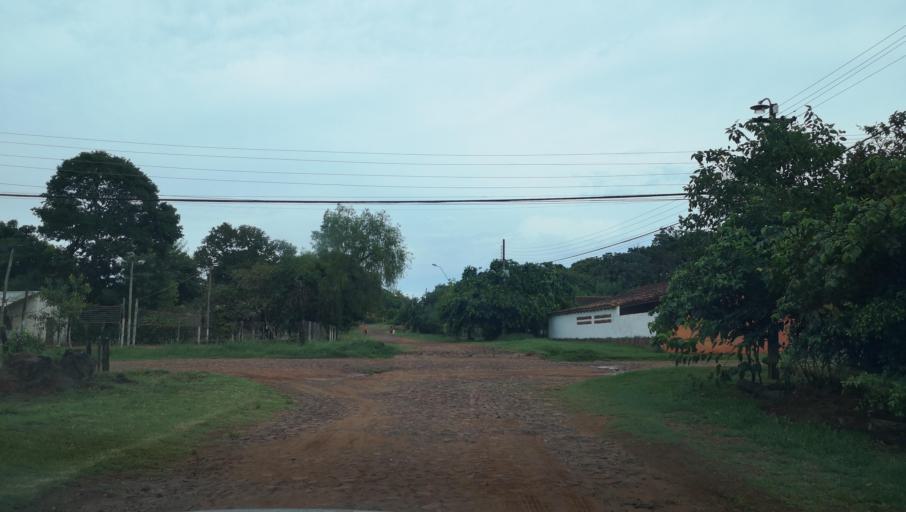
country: PY
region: Misiones
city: Santa Maria
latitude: -26.8827
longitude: -57.0264
